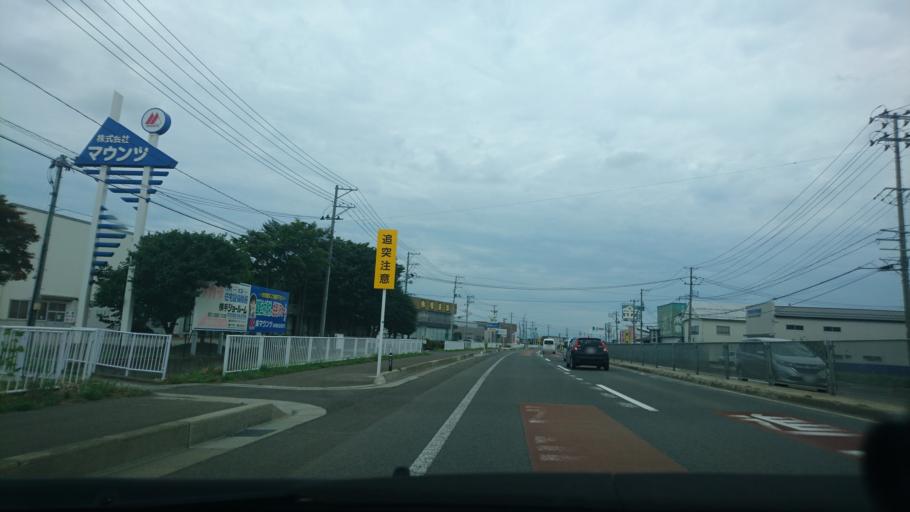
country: JP
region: Akita
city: Yokotemachi
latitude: 39.3210
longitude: 140.5547
